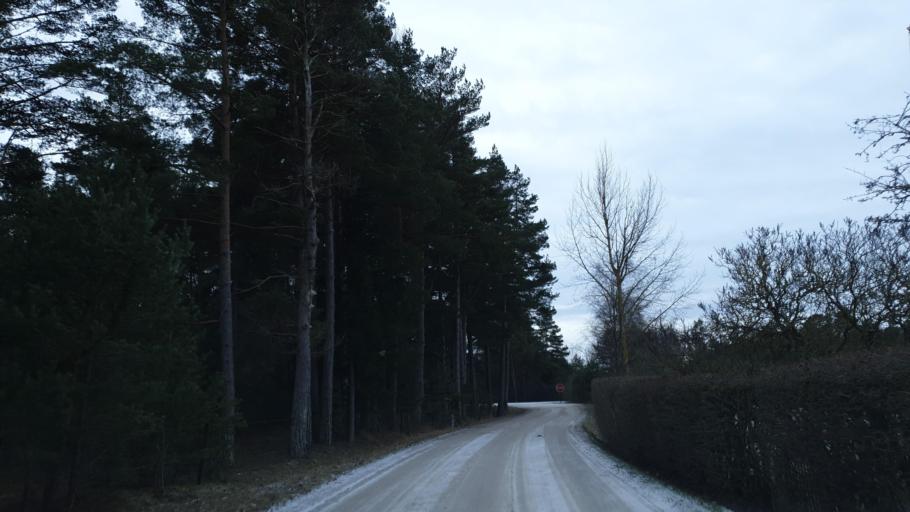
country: SE
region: Gotland
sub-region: Gotland
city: Slite
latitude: 57.4296
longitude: 18.8114
